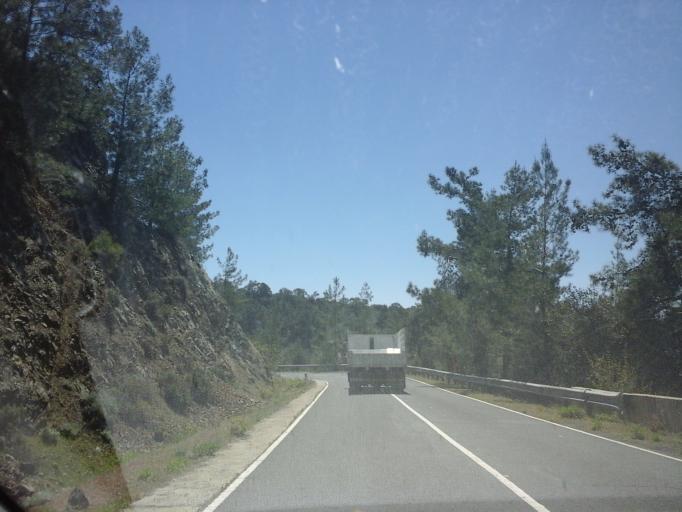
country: CY
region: Lefkosia
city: Kakopetria
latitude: 34.9965
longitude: 32.7923
